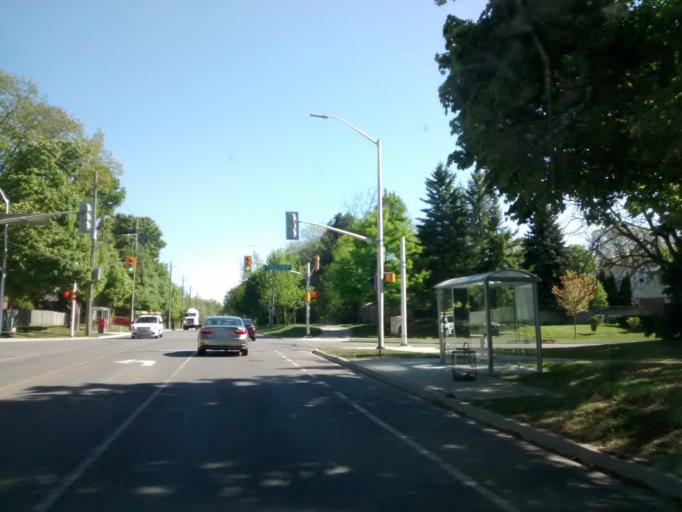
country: CA
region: Ontario
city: Oakville
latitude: 43.3846
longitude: -79.7172
